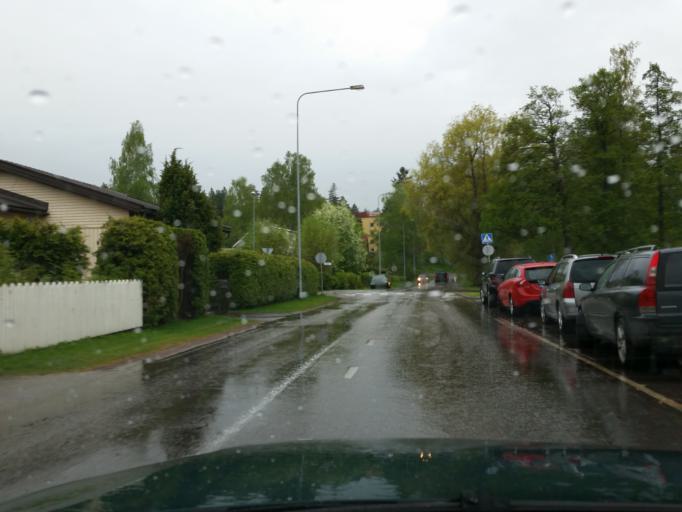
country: FI
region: Uusimaa
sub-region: Helsinki
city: Lohja
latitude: 60.2488
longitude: 24.0553
